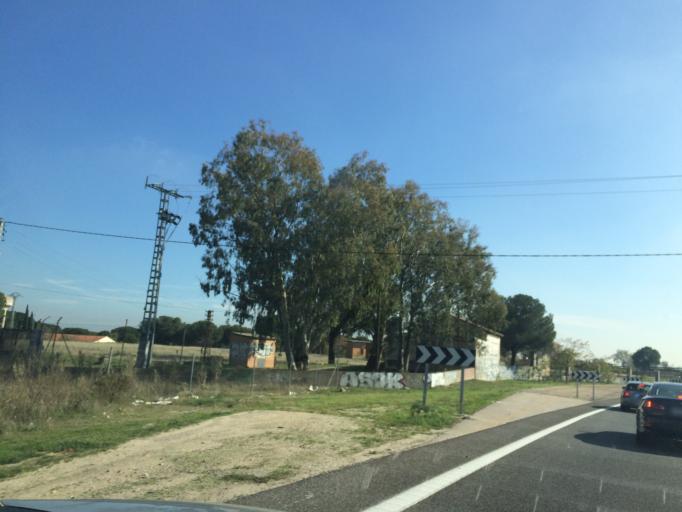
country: ES
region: Madrid
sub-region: Provincia de Madrid
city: Las Tablas
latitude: 40.5386
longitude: -3.6979
